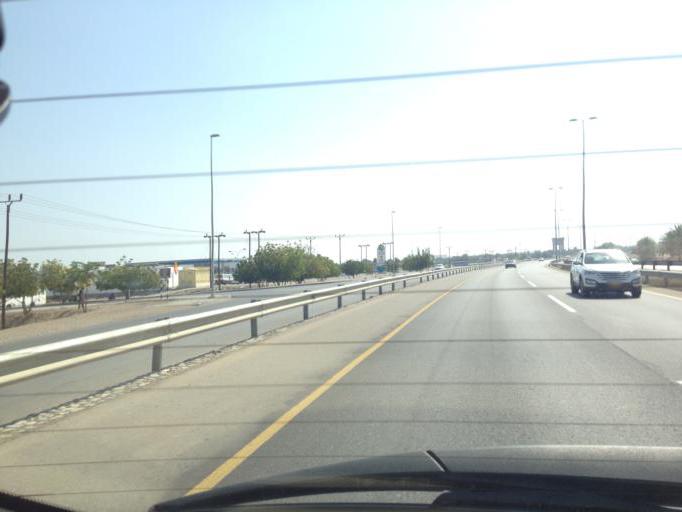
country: OM
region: Muhafazat Masqat
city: As Sib al Jadidah
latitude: 23.5900
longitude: 58.2418
